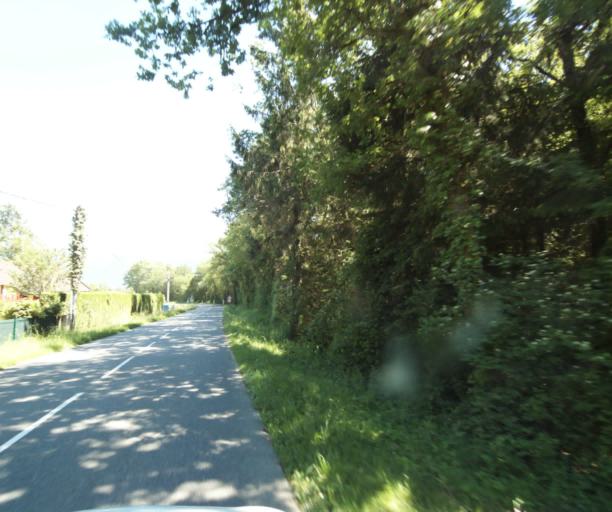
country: FR
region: Rhone-Alpes
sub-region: Departement de la Haute-Savoie
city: Ballaison
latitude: 46.2820
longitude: 6.3502
